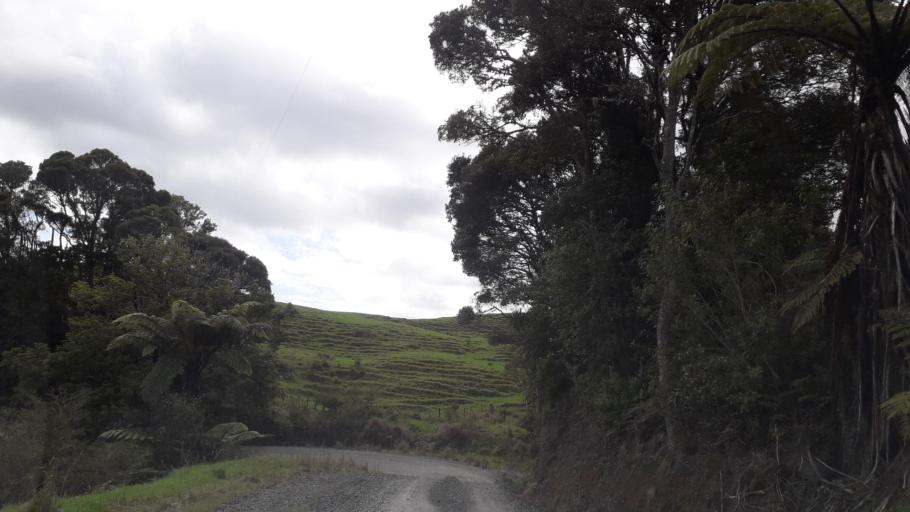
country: NZ
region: Northland
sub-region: Far North District
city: Kaitaia
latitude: -35.1906
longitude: 173.2916
